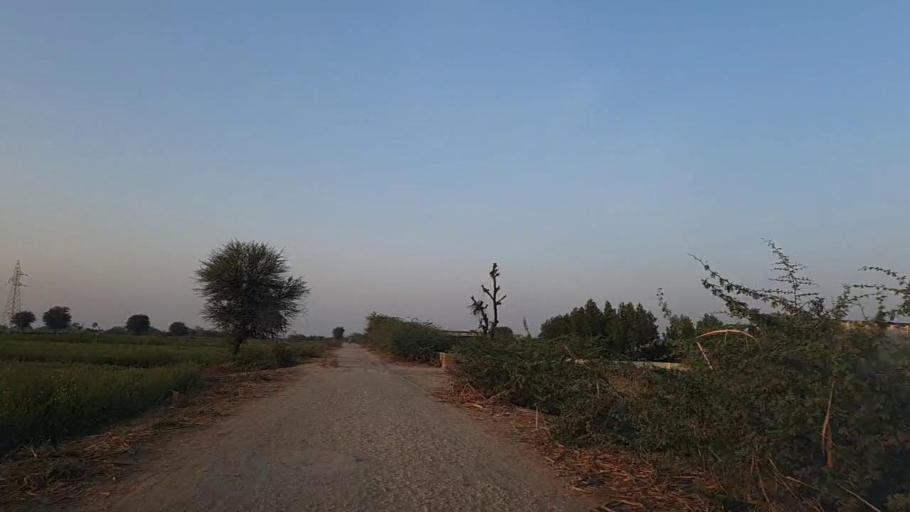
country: PK
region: Sindh
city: Naukot
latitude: 24.9498
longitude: 69.4370
